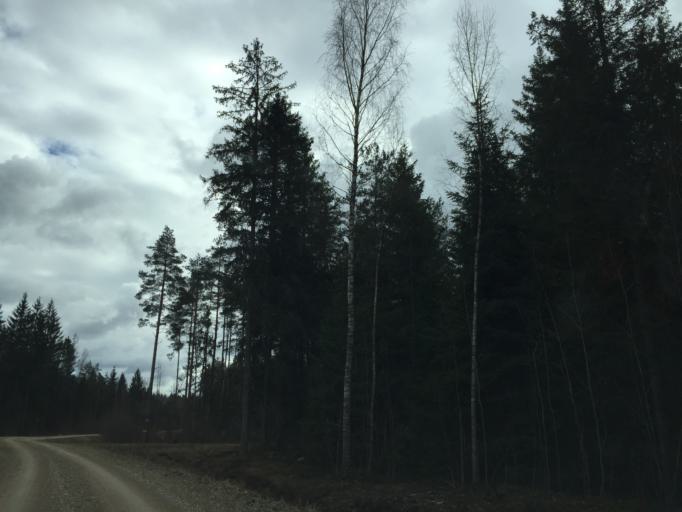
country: LV
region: Akniste
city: Akniste
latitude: 56.0928
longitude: 25.7613
